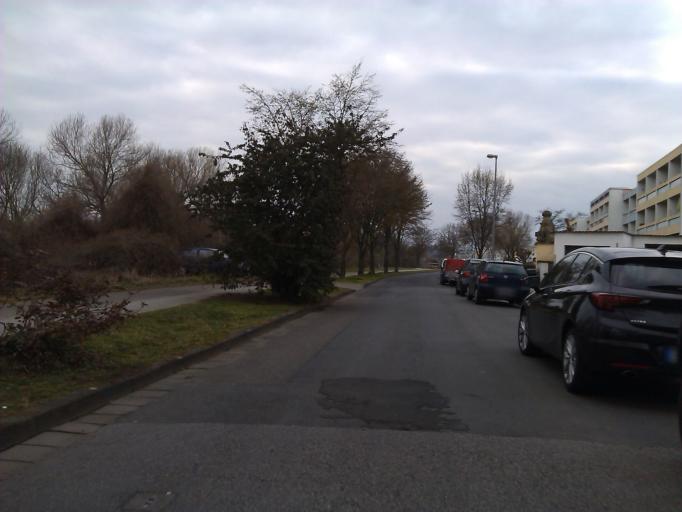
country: DE
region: Rheinland-Pfalz
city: Mainz
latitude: 50.0201
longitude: 8.2697
